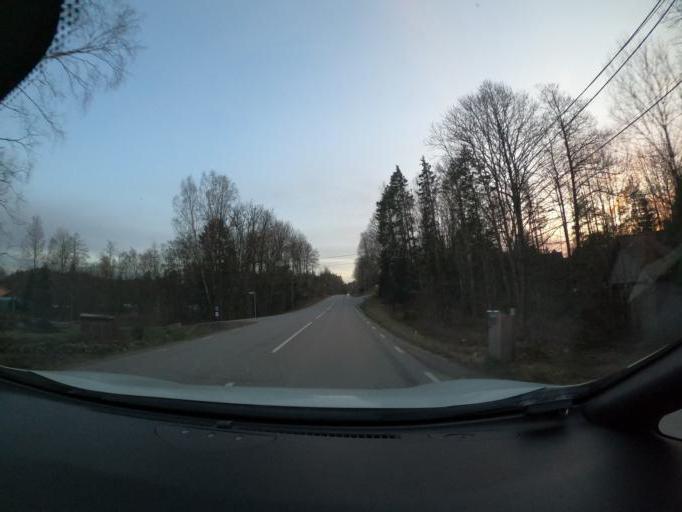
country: SE
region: Vaestra Goetaland
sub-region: Harryda Kommun
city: Landvetter
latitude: 57.6359
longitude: 12.1812
